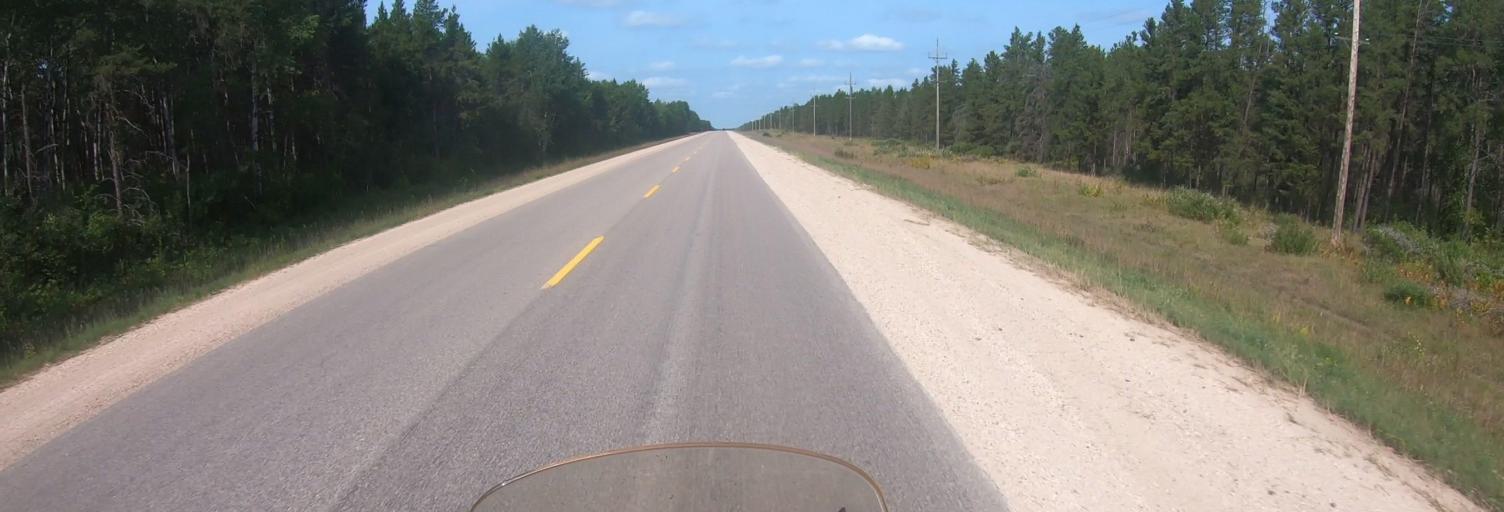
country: CA
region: Manitoba
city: La Broquerie
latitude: 49.1763
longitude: -96.1736
